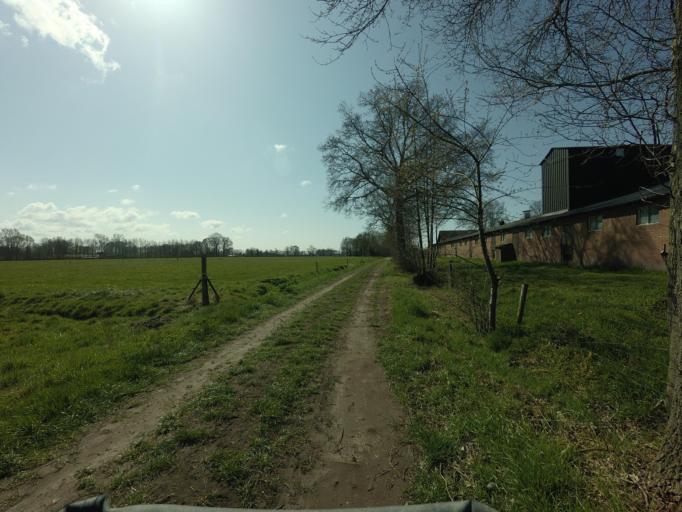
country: NL
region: Gelderland
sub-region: Gemeente Barneveld
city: Terschuur
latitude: 52.1389
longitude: 5.5156
